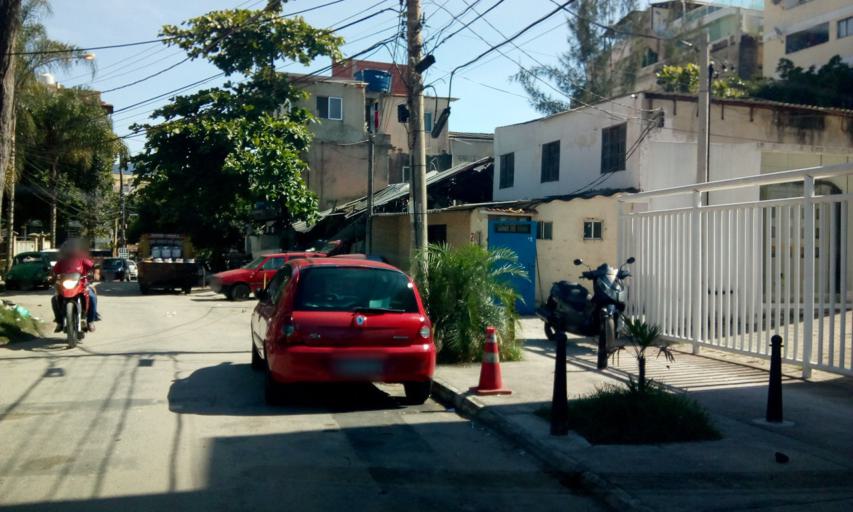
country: BR
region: Rio de Janeiro
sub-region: Nilopolis
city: Nilopolis
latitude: -23.0294
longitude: -43.4739
